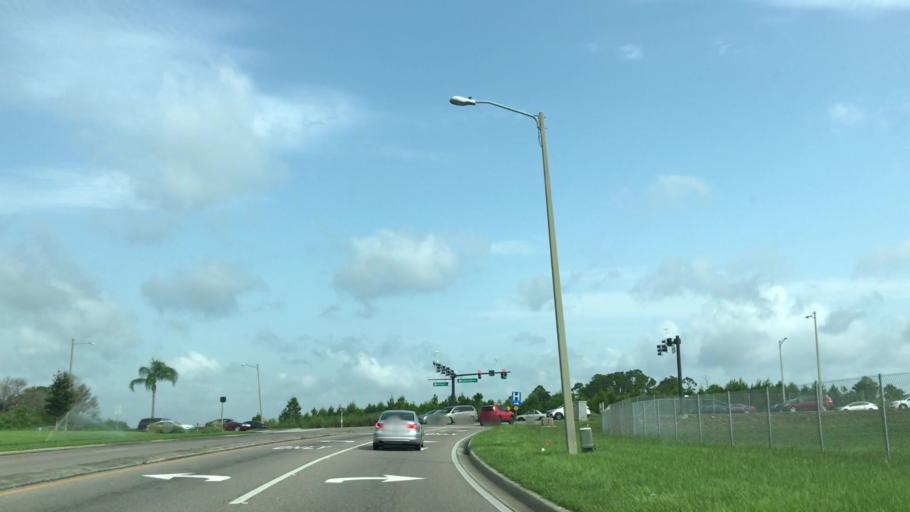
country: US
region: Florida
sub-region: Orange County
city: Williamsburg
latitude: 28.4108
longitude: -81.4764
